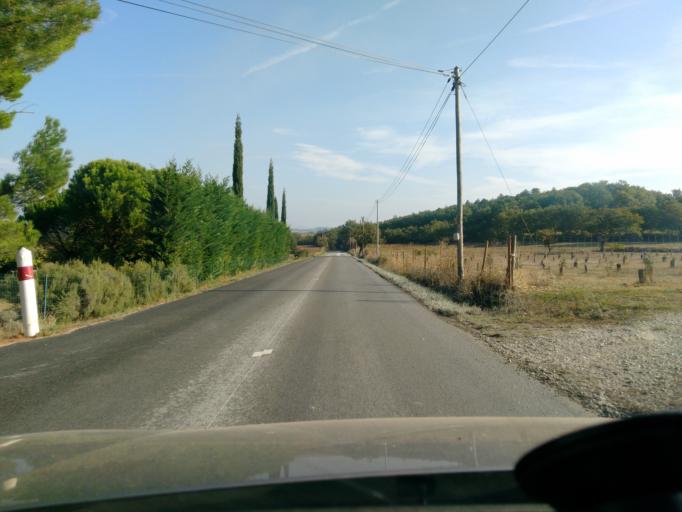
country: FR
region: Rhone-Alpes
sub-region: Departement de la Drome
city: Montboucher-sur-Jabron
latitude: 44.5408
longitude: 4.8374
